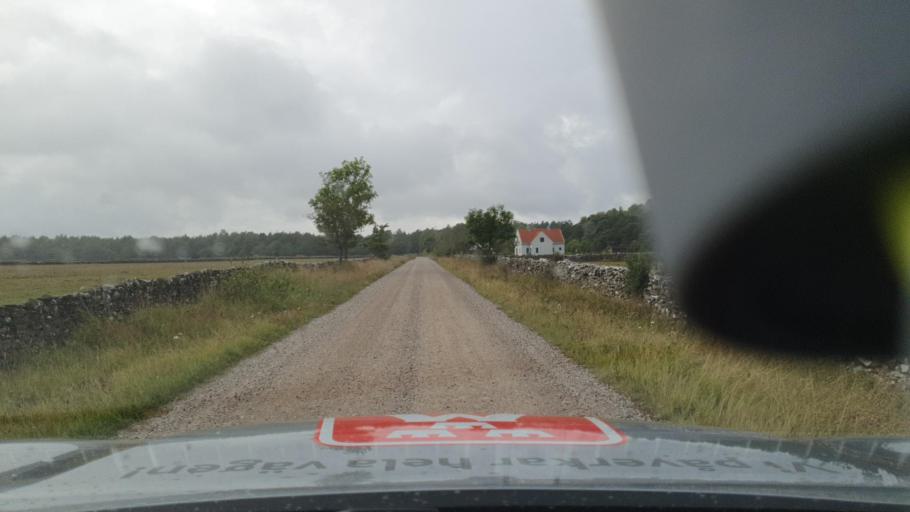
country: SE
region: Gotland
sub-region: Gotland
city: Hemse
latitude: 56.9999
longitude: 18.3166
